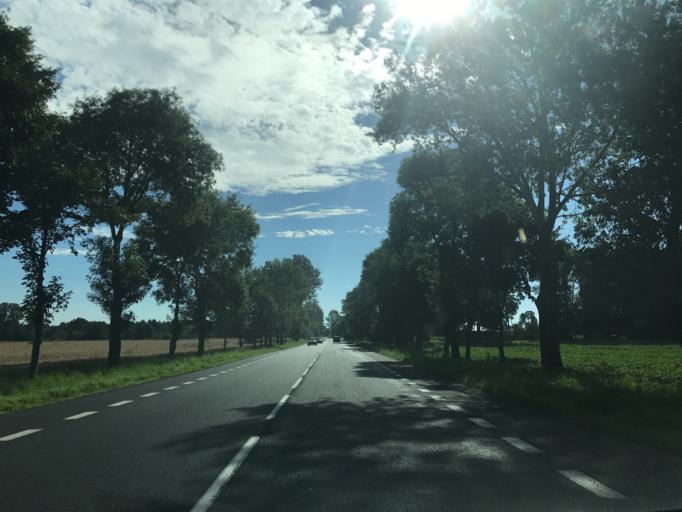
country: PL
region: West Pomeranian Voivodeship
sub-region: Powiat slawienski
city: Slawno
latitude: 54.3384
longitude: 16.6228
